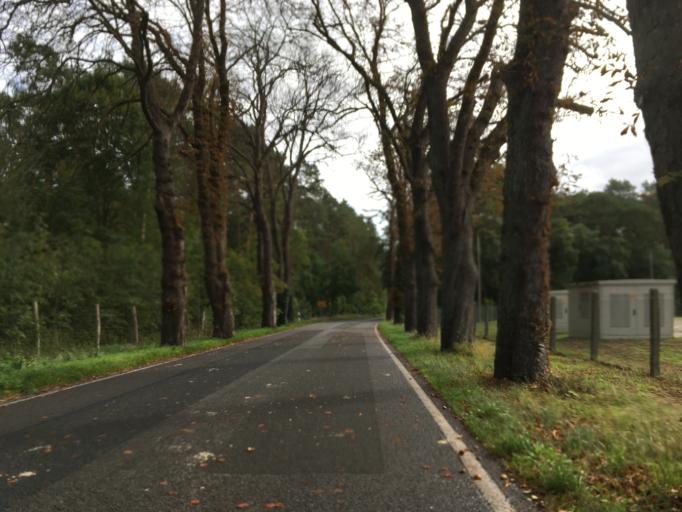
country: DE
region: Brandenburg
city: Oderberg
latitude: 52.8916
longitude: 14.0618
